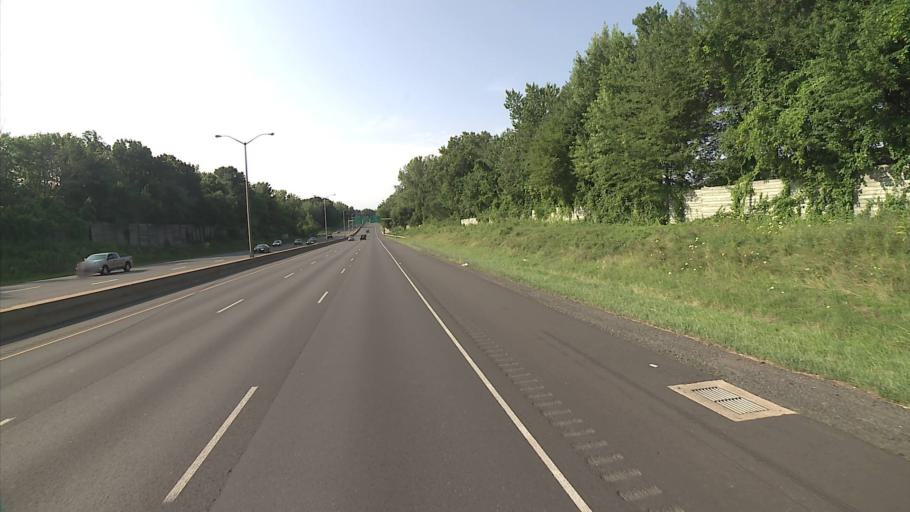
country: US
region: Connecticut
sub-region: Hartford County
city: Thompsonville
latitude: 42.0093
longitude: -72.5860
